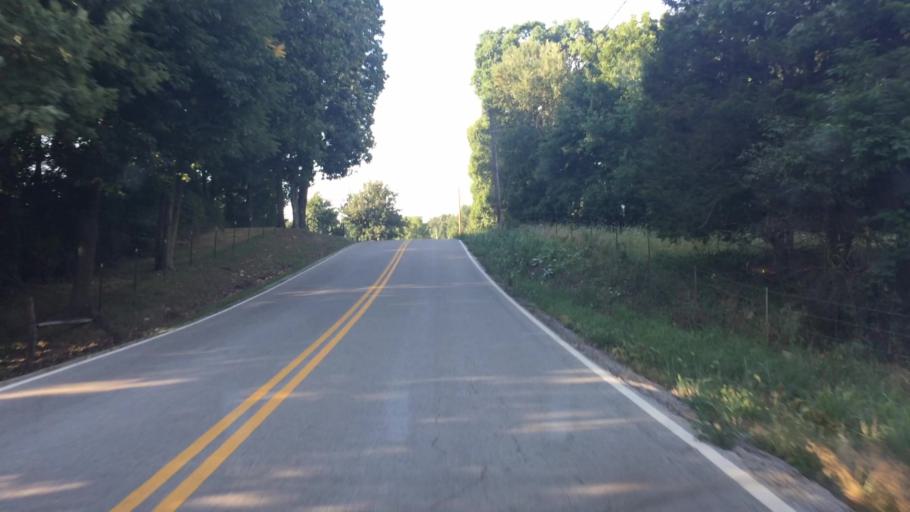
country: US
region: Missouri
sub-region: Greene County
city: Strafford
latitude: 37.2594
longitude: -93.1878
